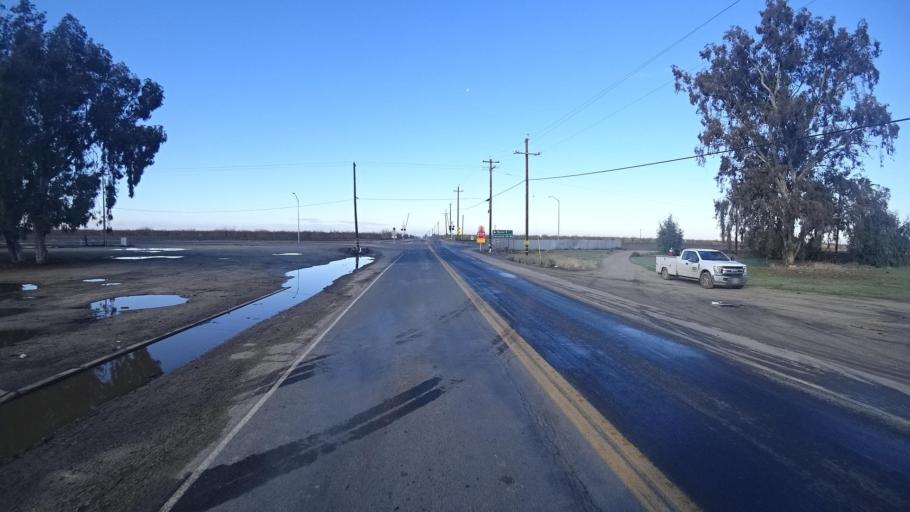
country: US
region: California
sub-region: Kern County
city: Delano
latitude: 35.7177
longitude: -119.3297
